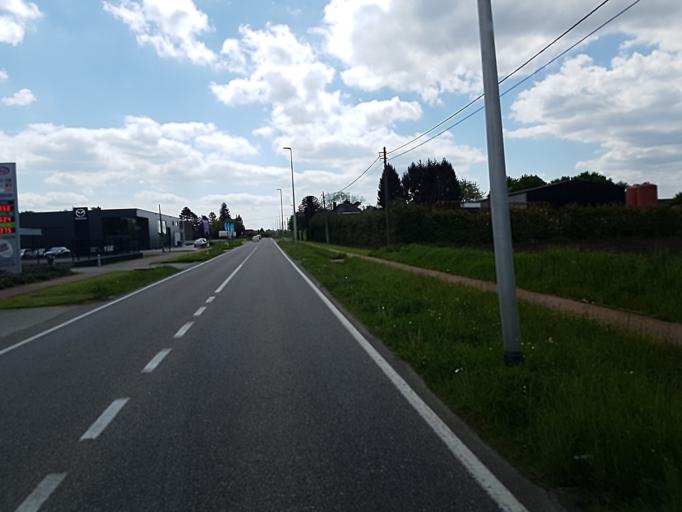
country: BE
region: Flanders
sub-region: Provincie Antwerpen
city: Laakdal
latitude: 51.0714
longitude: 4.9649
